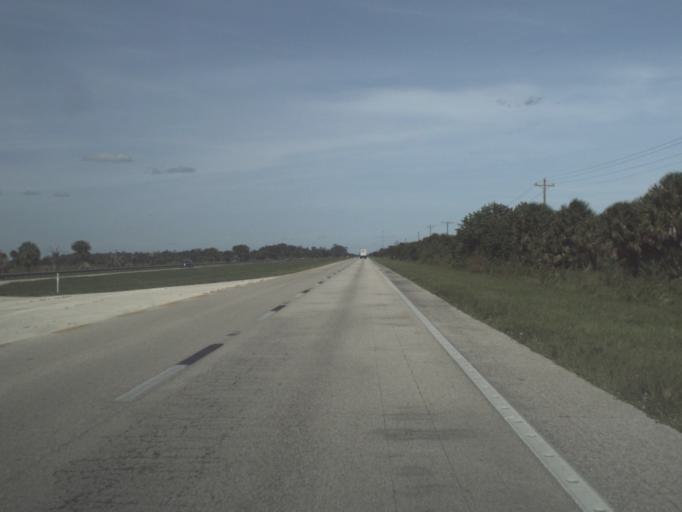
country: US
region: Florida
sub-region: Glades County
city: Moore Haven
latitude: 26.8444
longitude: -81.1987
